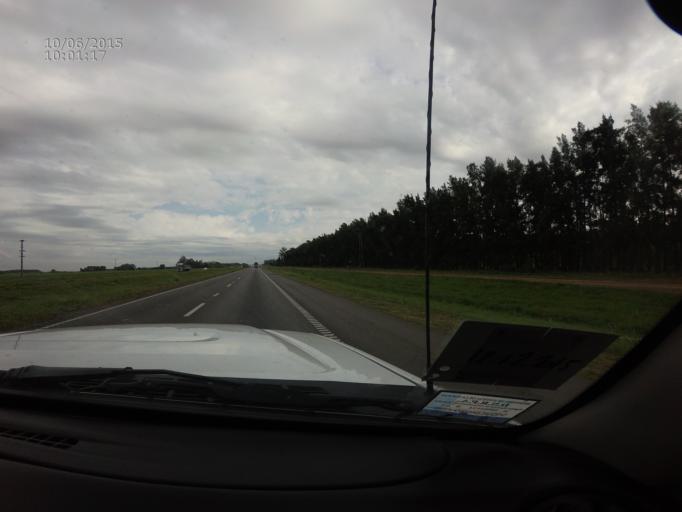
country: AR
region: Buenos Aires
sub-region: Partido de Baradero
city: Baradero
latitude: -33.8857
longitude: -59.4933
